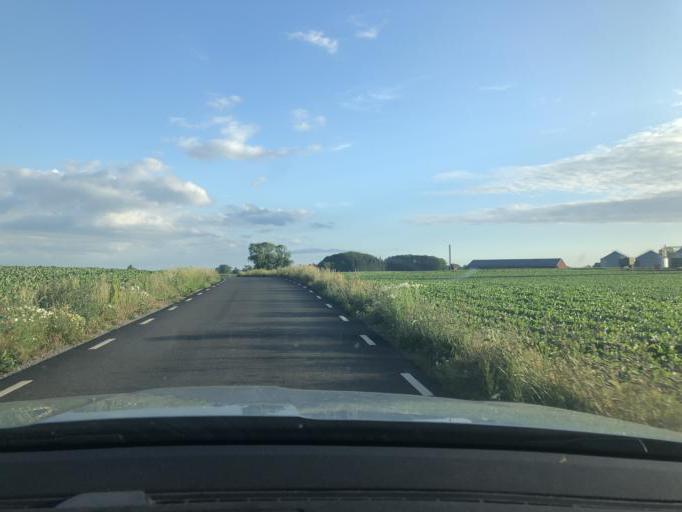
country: SE
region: Skane
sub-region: Simrishamns Kommun
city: Simrishamn
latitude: 55.4710
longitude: 14.1921
